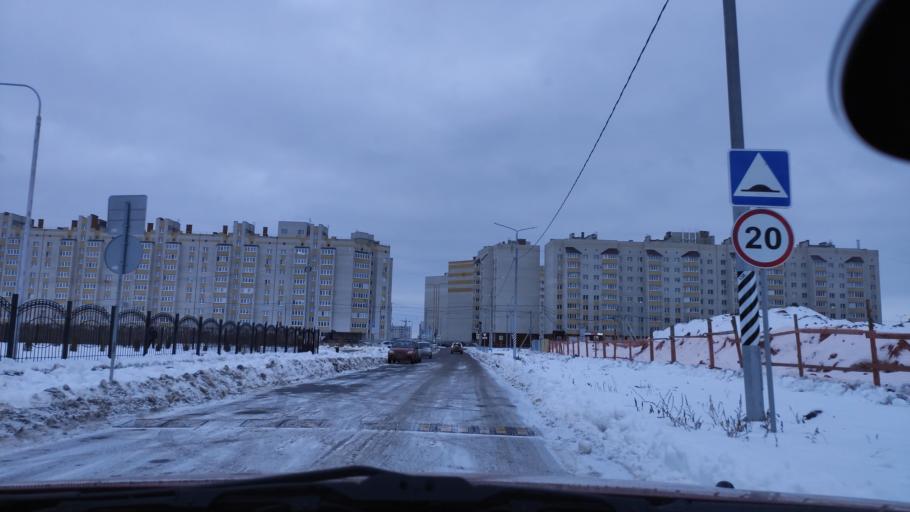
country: RU
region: Tambov
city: Tambov
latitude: 52.7782
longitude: 41.4100
